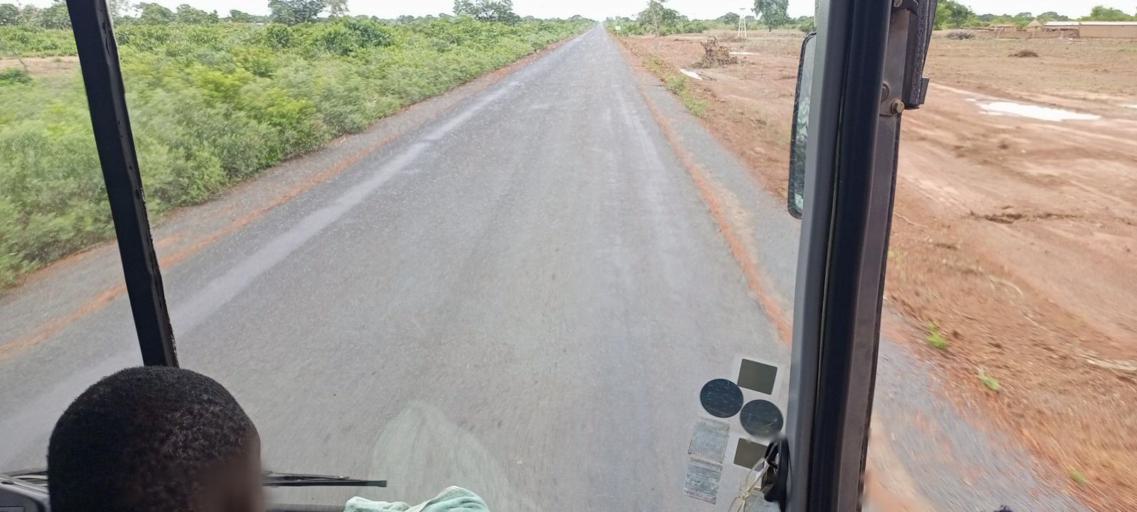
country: ML
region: Sikasso
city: Koutiala
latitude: 12.5678
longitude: -5.5996
